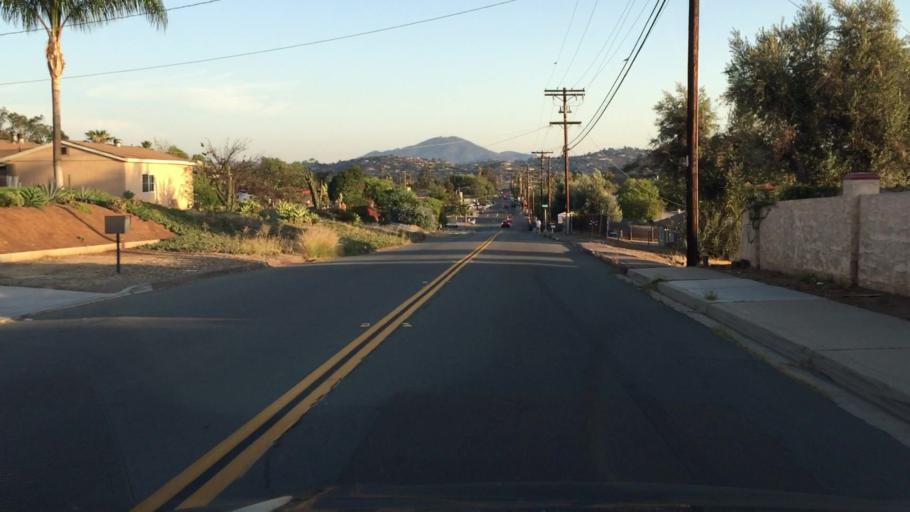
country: US
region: California
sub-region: San Diego County
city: Bostonia
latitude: 32.8160
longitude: -116.9447
